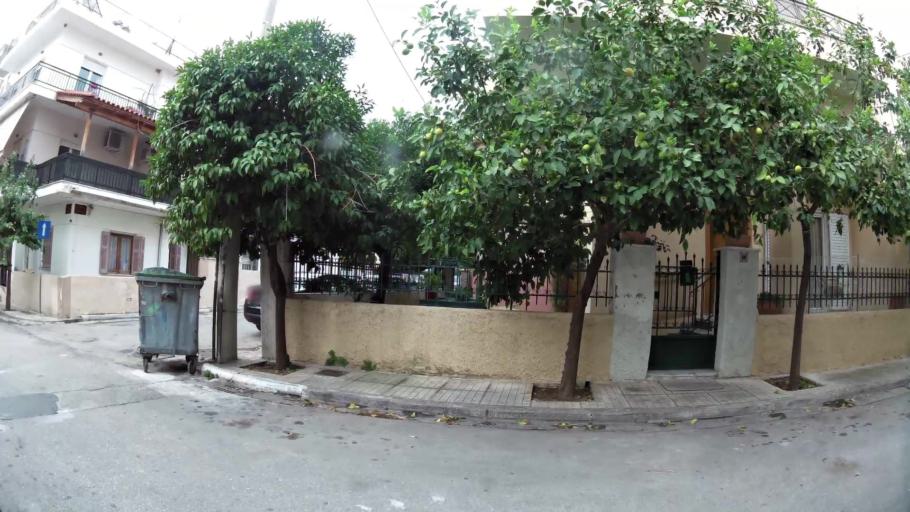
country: GR
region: Attica
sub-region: Nomarchia Athinas
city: Chaidari
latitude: 38.0093
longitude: 23.6662
